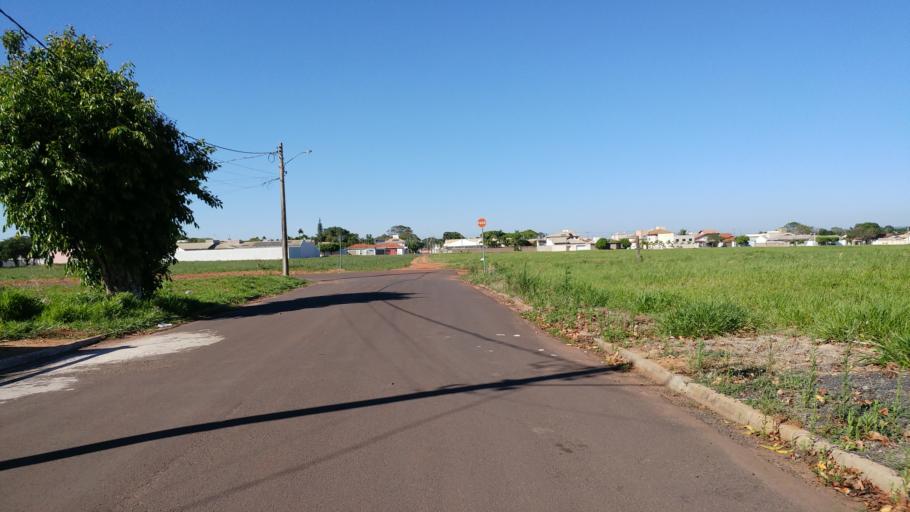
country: BR
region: Sao Paulo
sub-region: Paraguacu Paulista
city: Paraguacu Paulista
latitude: -22.4080
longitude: -50.5839
